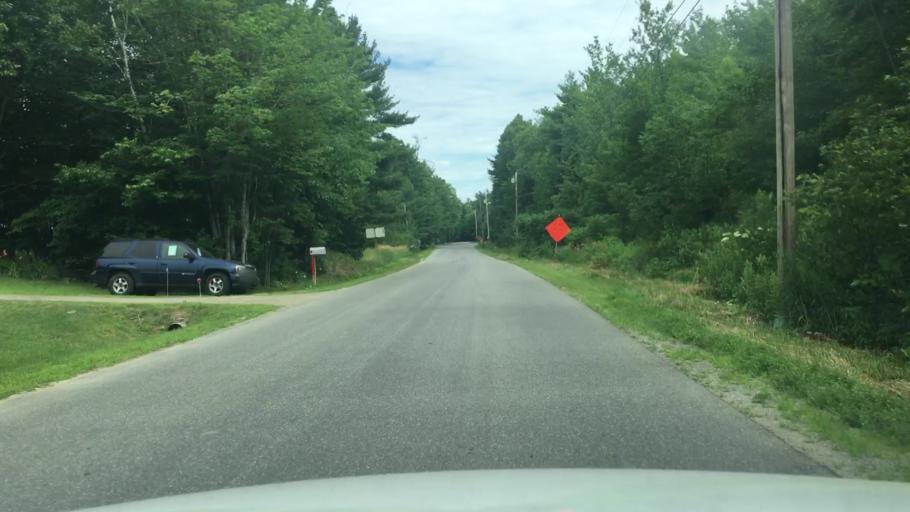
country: US
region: Maine
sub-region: Kennebec County
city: Clinton
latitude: 44.6004
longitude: -69.4722
